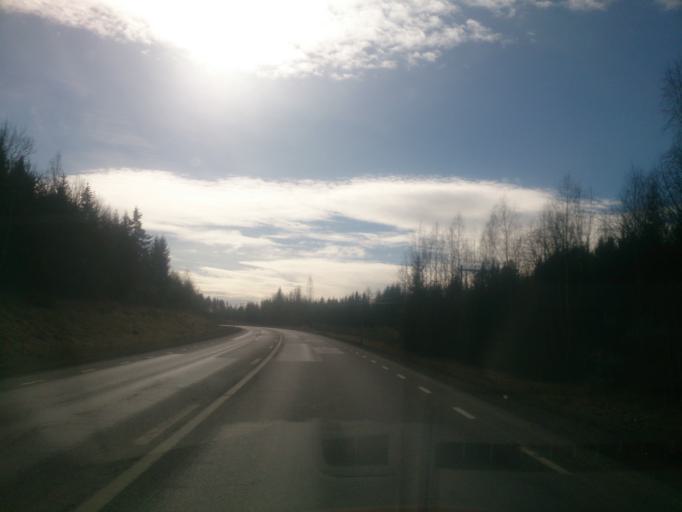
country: SE
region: OEstergoetland
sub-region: Norrkopings Kommun
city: Kimstad
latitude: 58.5349
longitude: 15.9767
